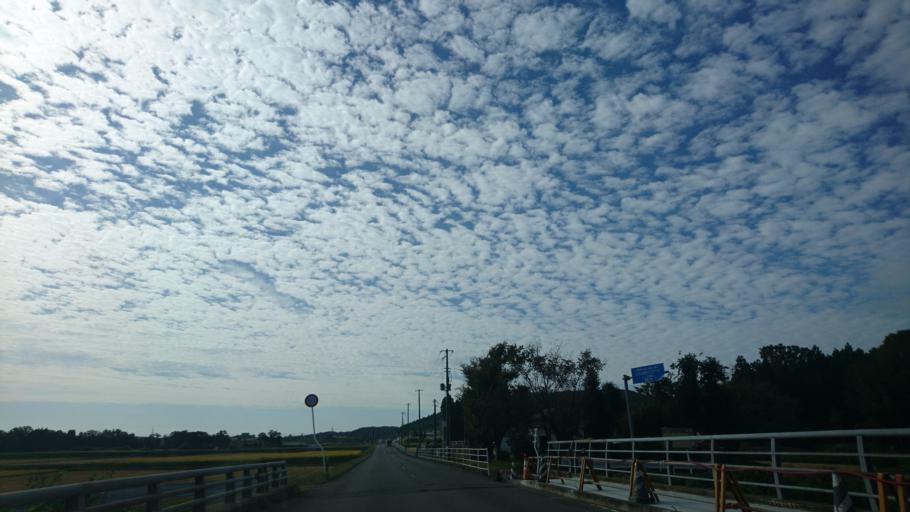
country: JP
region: Fukushima
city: Sukagawa
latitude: 37.3255
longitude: 140.2670
